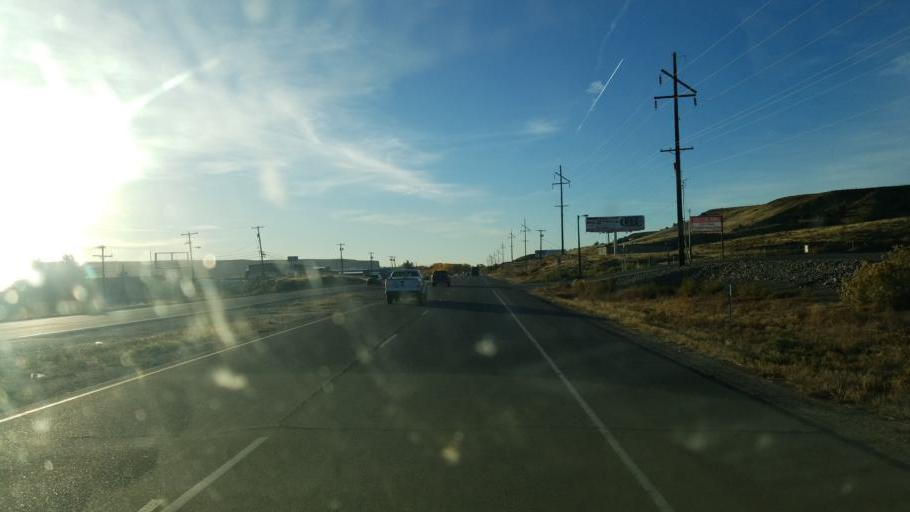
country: US
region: New Mexico
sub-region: San Juan County
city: Lee Acres
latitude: 36.7054
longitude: -108.1126
